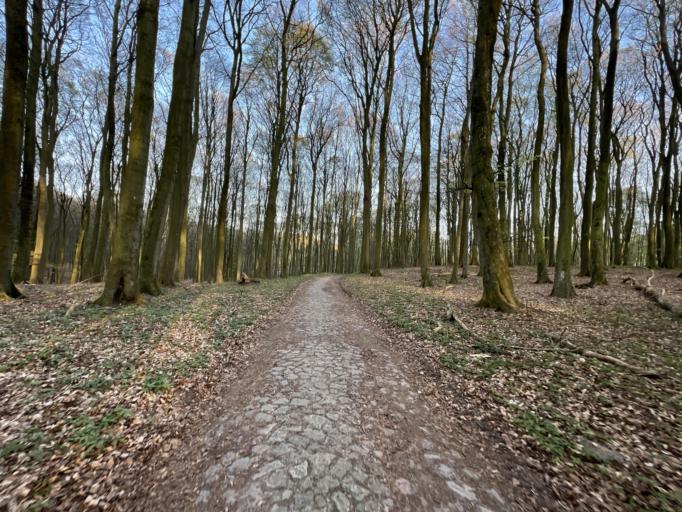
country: DE
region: Mecklenburg-Vorpommern
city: Sassnitz
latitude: 54.5313
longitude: 13.6530
